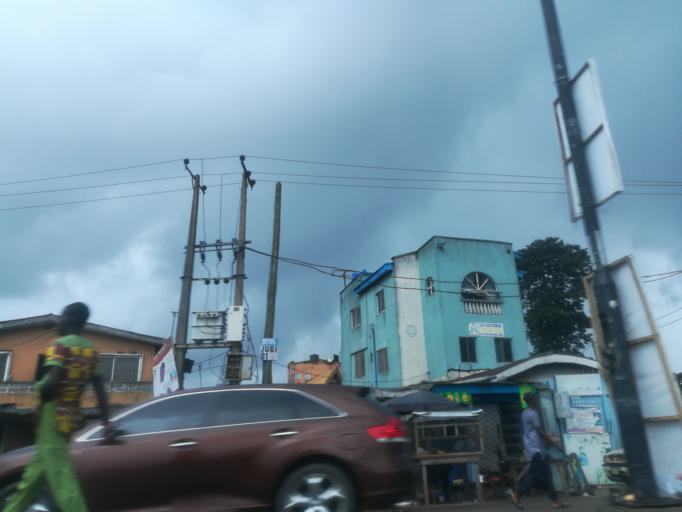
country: NG
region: Lagos
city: Agege
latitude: 6.6172
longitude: 3.3212
